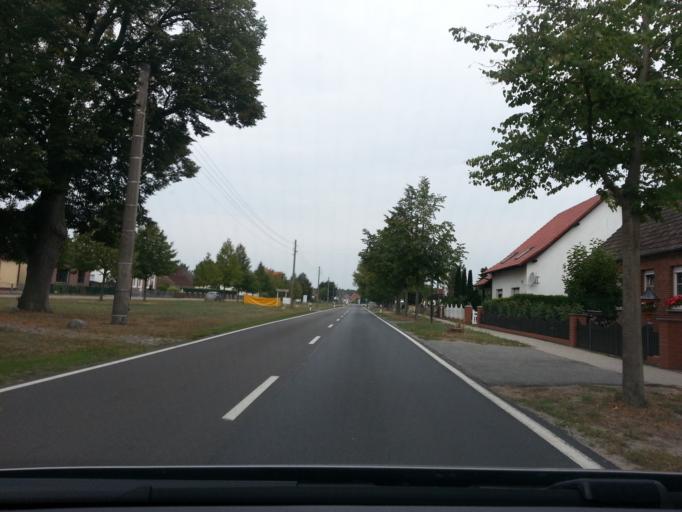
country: DE
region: Mecklenburg-Vorpommern
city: Ferdinandshof
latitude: 53.7035
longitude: 13.9421
